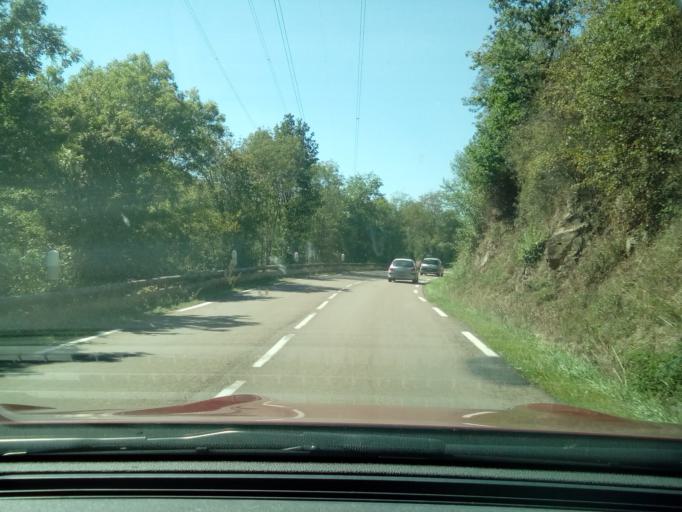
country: FR
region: Rhone-Alpes
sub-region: Departement du Rhone
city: Saint-Verand
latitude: 45.9079
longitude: 4.5197
